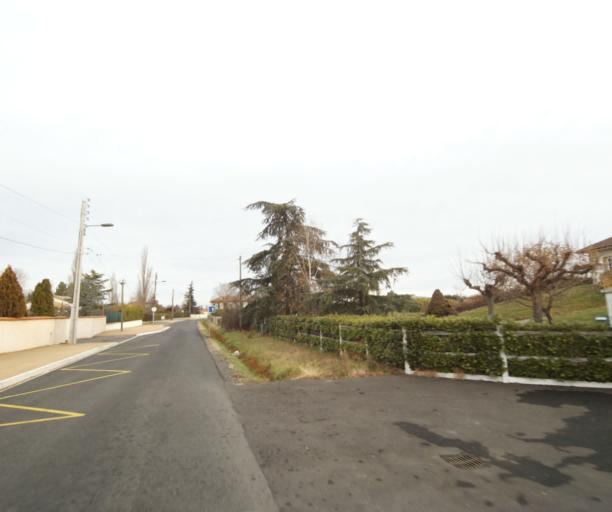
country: FR
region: Rhone-Alpes
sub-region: Departement de la Loire
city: Sury-le-Comtal
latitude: 45.5225
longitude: 4.1821
